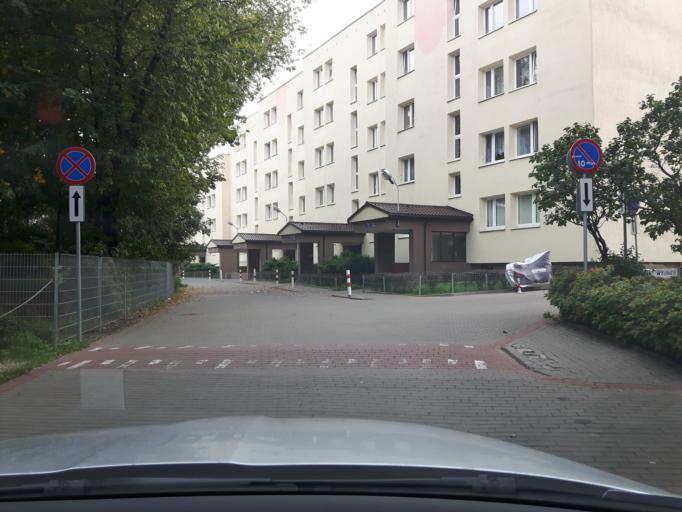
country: PL
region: Masovian Voivodeship
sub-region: Warszawa
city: Praga Polnoc
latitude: 52.2678
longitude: 21.0476
